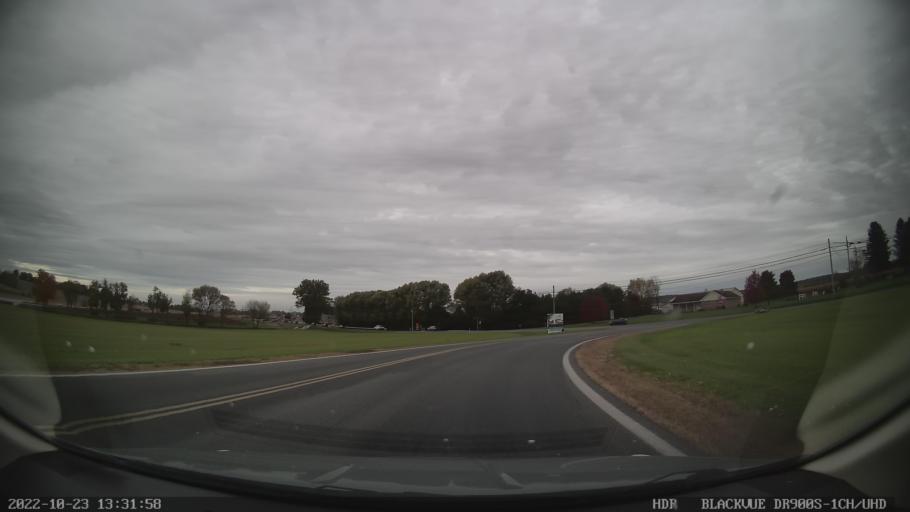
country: US
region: Pennsylvania
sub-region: Lehigh County
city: Breinigsville
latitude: 40.5457
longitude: -75.6698
